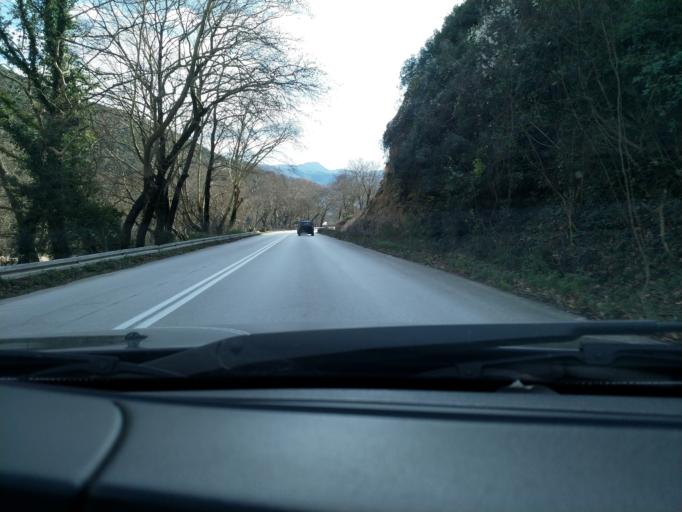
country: GR
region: Epirus
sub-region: Nomos Prevezis
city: Pappadates
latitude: 39.3957
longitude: 20.8524
